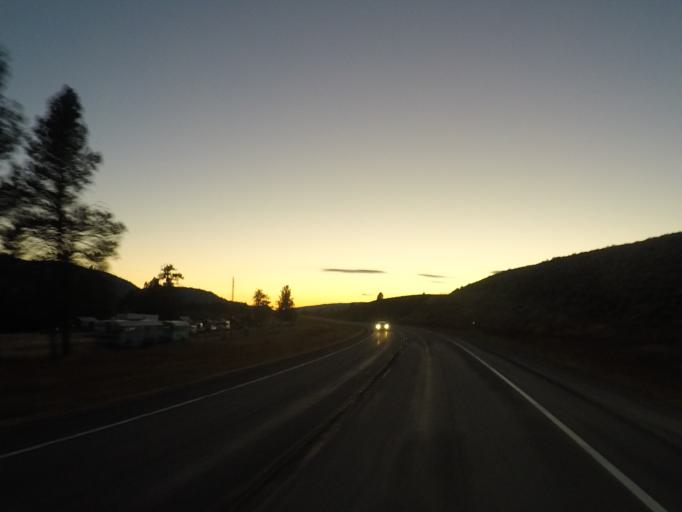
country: US
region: Montana
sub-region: Missoula County
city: Seeley Lake
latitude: 47.0431
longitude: -113.2120
